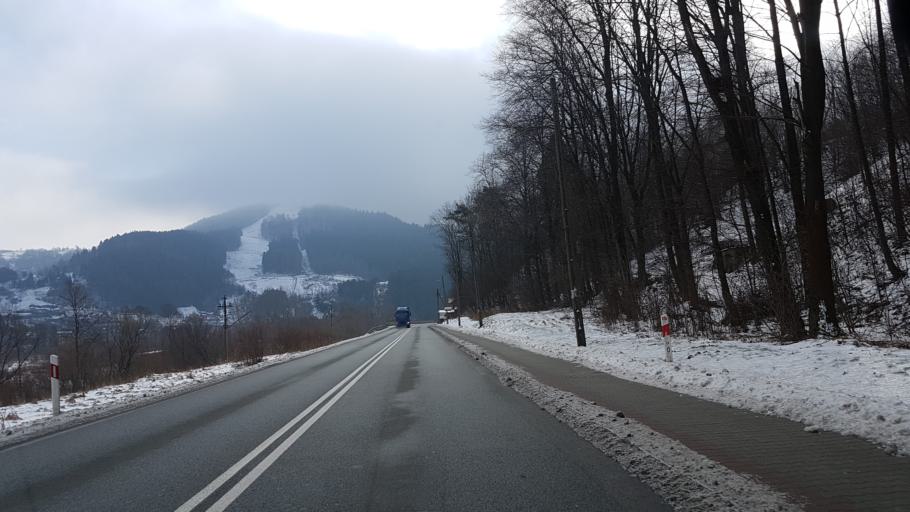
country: PL
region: Lesser Poland Voivodeship
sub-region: Powiat nowosadecki
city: Piwniczna-Zdroj
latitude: 49.4448
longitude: 20.7118
